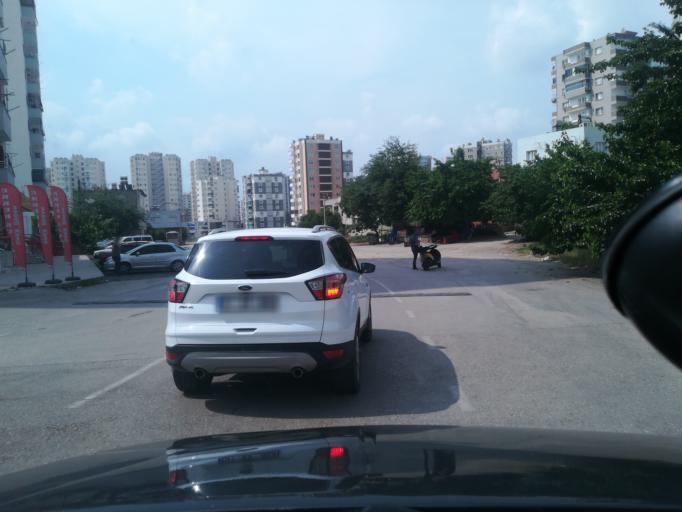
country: TR
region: Adana
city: Seyhan
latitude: 37.0275
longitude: 35.2805
